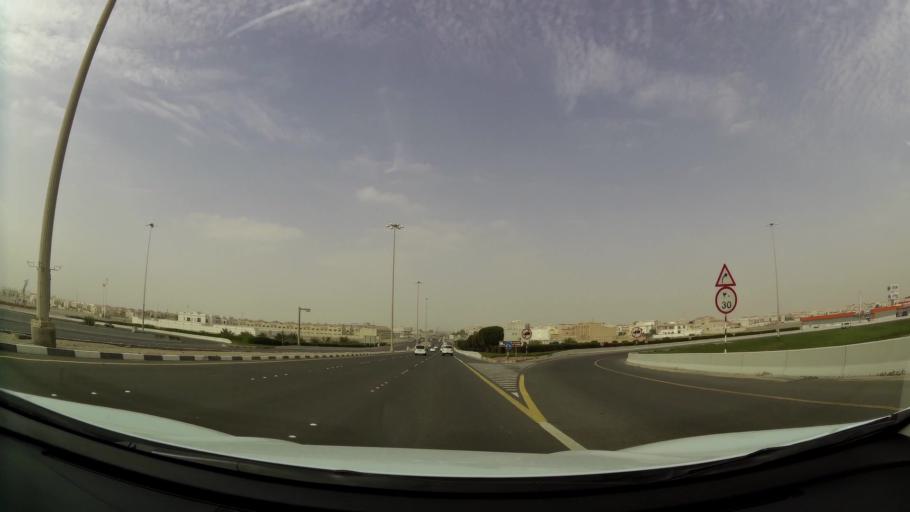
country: AE
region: Abu Dhabi
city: Abu Dhabi
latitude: 24.3987
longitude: 54.5740
